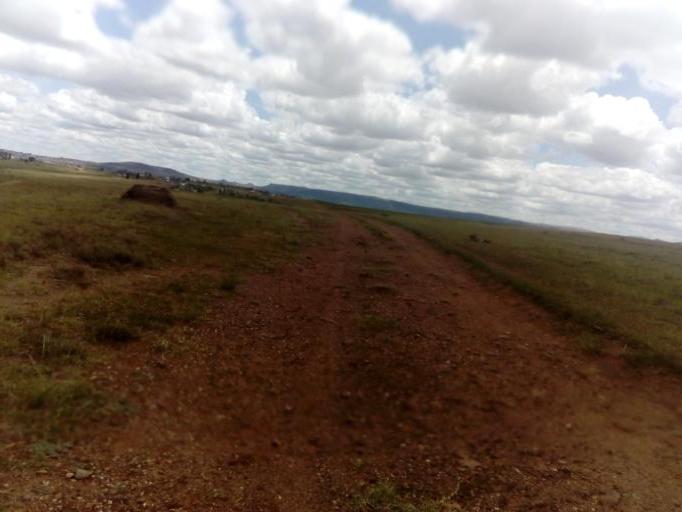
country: LS
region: Berea
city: Teyateyaneng
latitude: -29.1224
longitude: 27.7609
